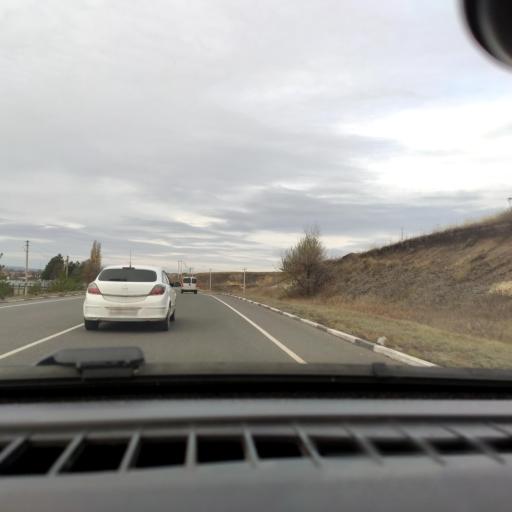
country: RU
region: Belgorod
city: Alekseyevka
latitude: 50.6422
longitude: 38.6552
